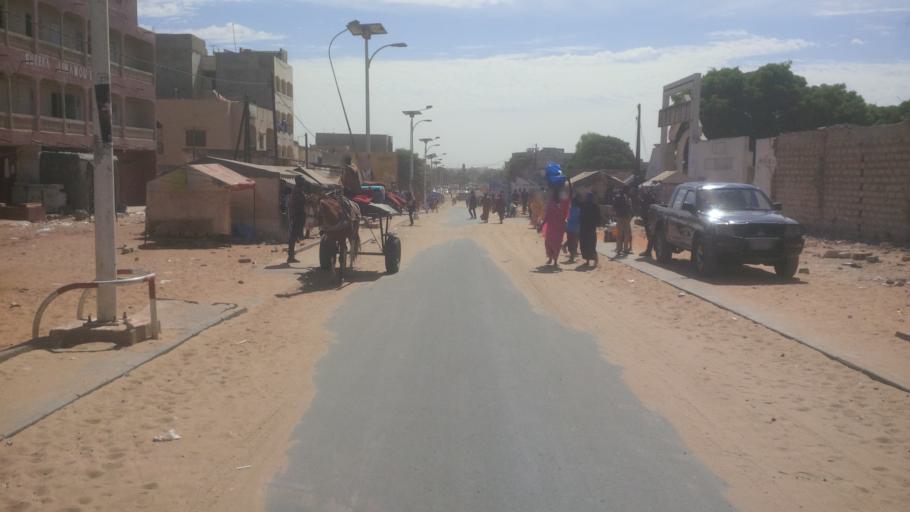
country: SN
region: Dakar
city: Pikine
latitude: 14.7781
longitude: -17.3793
